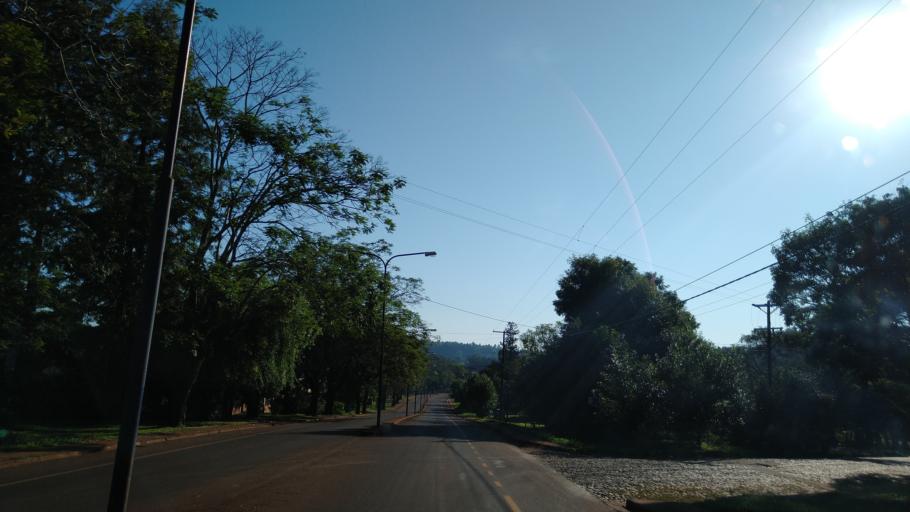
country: AR
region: Misiones
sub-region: Departamento de Montecarlo
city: Montecarlo
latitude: -26.5740
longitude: -54.7445
